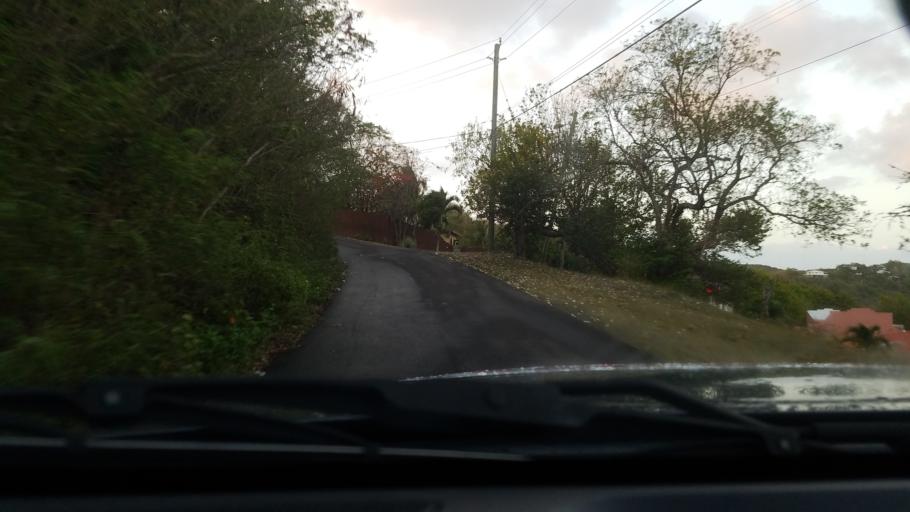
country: LC
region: Gros-Islet
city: Gros Islet
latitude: 14.0927
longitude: -60.9407
